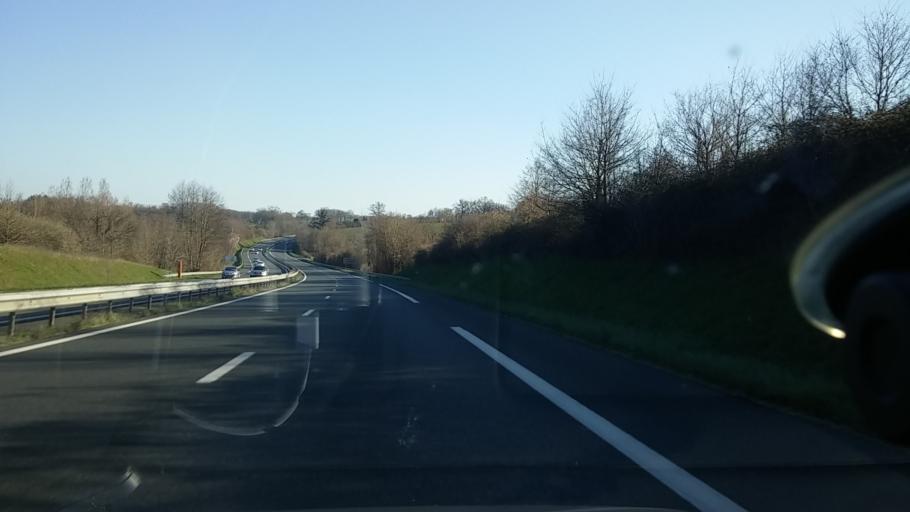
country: FR
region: Centre
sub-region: Departement de l'Indre
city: Chantome
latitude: 46.4663
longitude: 1.4966
